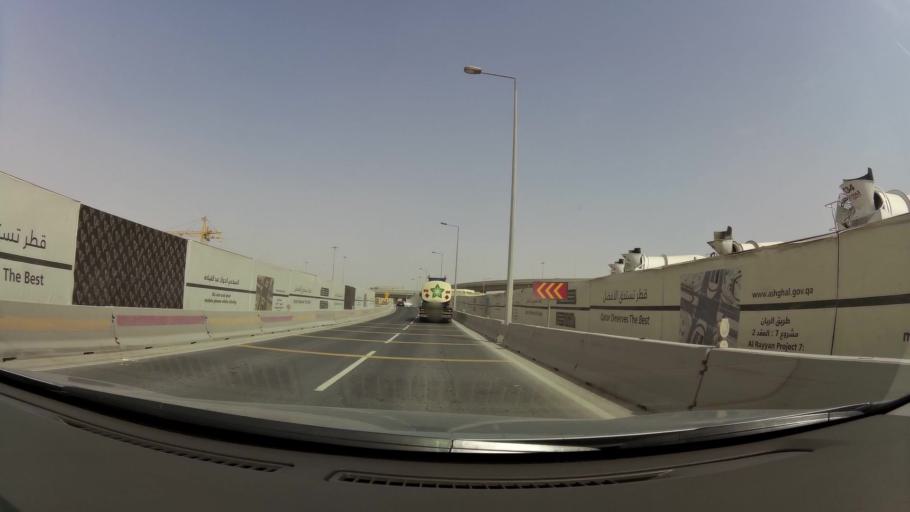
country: QA
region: Baladiyat ad Dawhah
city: Doha
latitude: 25.2931
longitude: 51.4765
